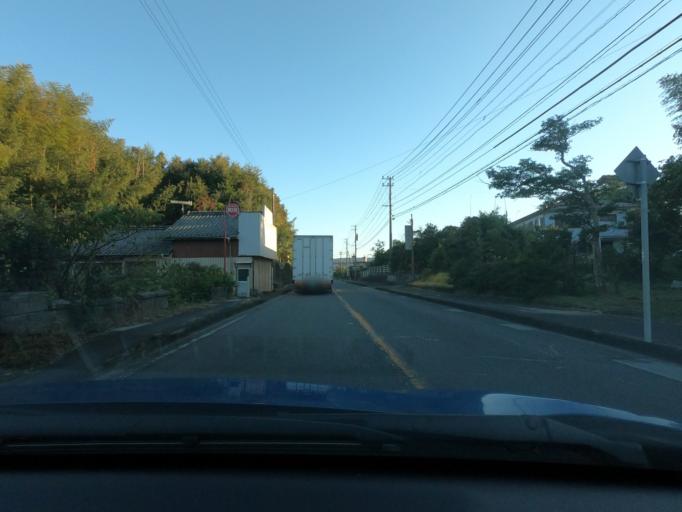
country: JP
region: Kagoshima
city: Satsumasendai
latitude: 31.8403
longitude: 130.2826
